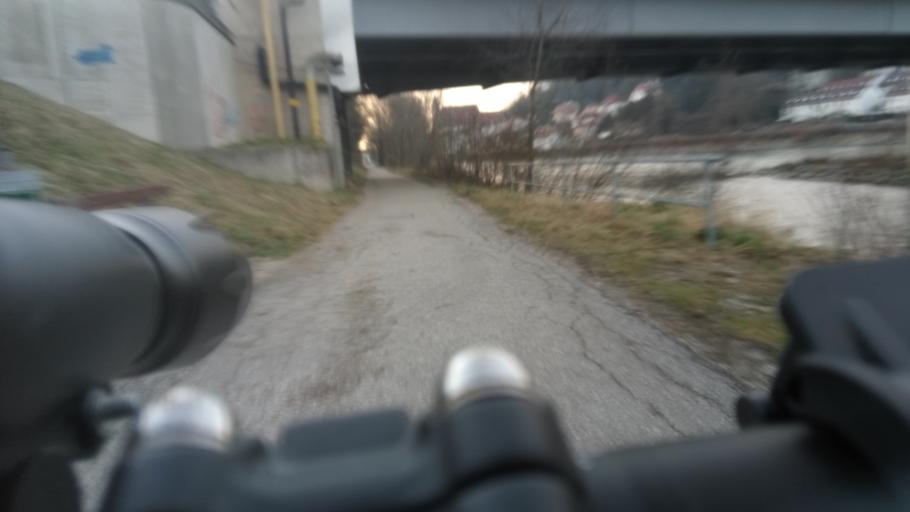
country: AT
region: Upper Austria
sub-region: Steyr Stadt
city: Steyr
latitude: 48.0429
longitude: 14.4304
